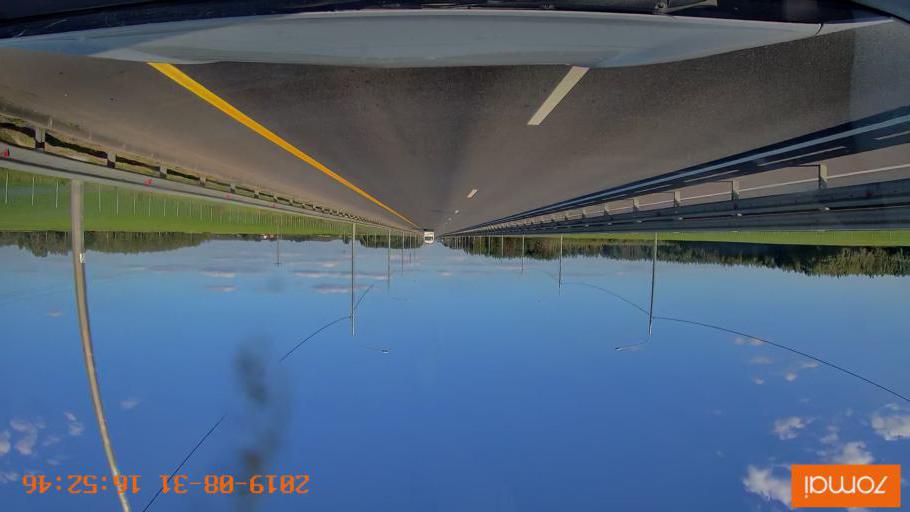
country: RU
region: Kaluga
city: Detchino
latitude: 54.7462
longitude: 36.1983
